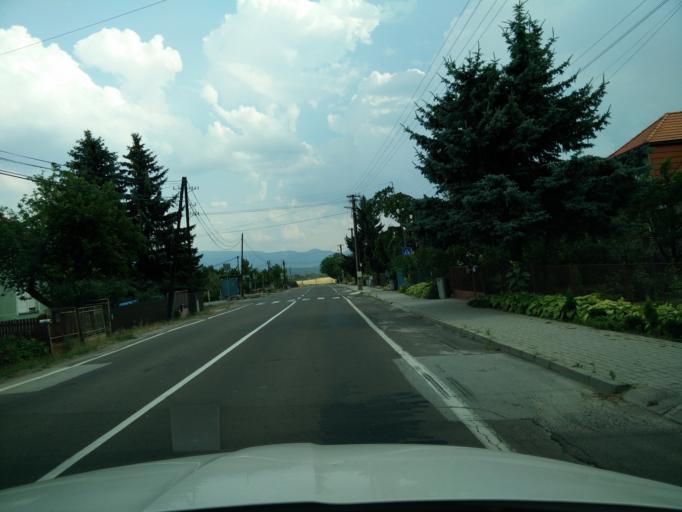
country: SK
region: Nitriansky
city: Novaky
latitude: 48.7643
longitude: 18.4952
